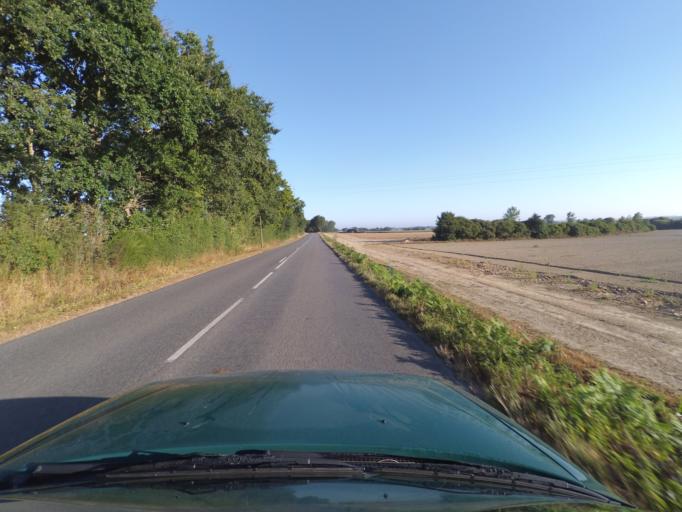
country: FR
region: Pays de la Loire
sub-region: Departement de la Loire-Atlantique
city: Vieillevigne
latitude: 46.9925
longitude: -1.4499
